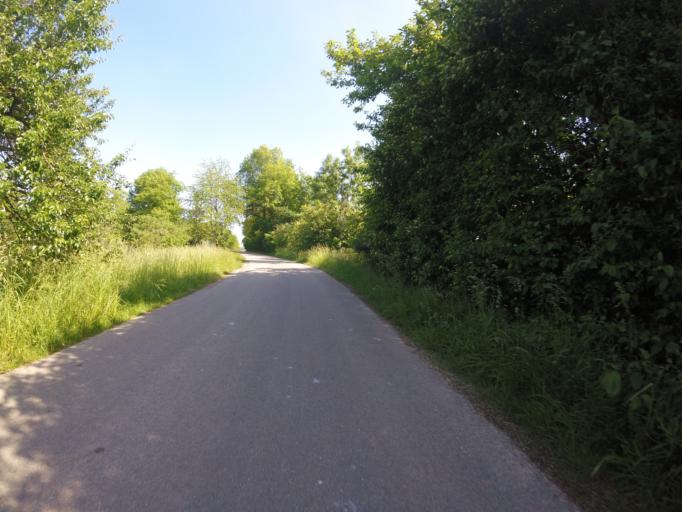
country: DE
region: Baden-Wuerttemberg
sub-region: Regierungsbezirk Stuttgart
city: Kirchberg an der Murr
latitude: 48.9668
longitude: 9.3258
